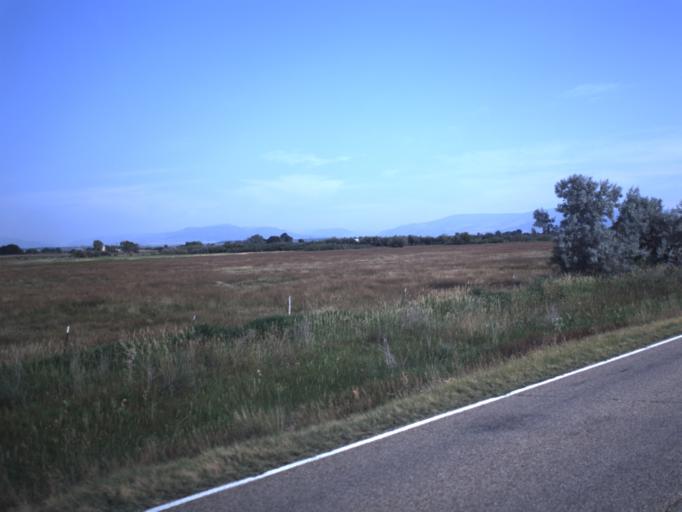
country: US
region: Utah
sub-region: Duchesne County
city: Duchesne
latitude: 40.3370
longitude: -110.2752
